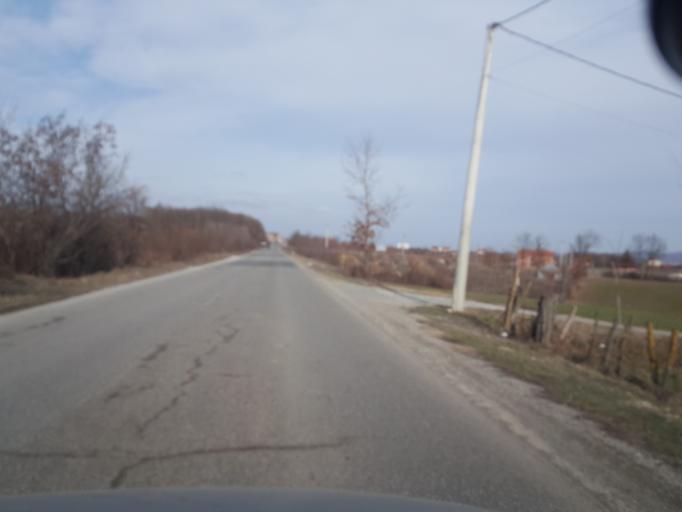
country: XK
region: Gjakova
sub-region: Komuna e Gjakoves
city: Gjakove
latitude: 42.4220
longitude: 20.4380
